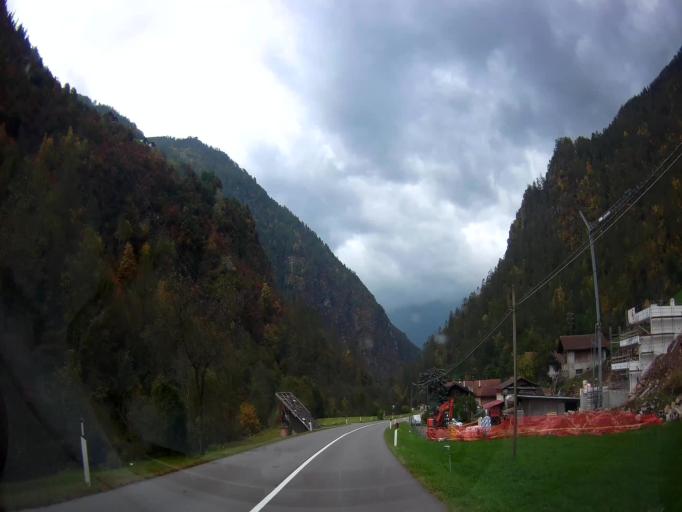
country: IT
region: Trentino-Alto Adige
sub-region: Bolzano
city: Certosa
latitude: 46.6726
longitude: 10.9425
